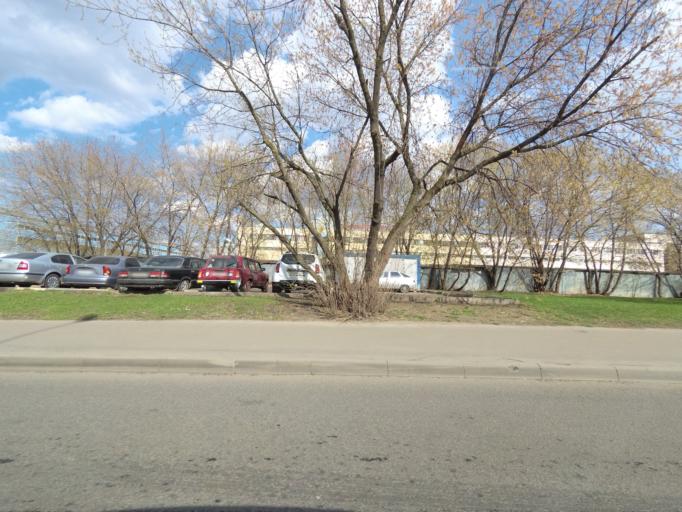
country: RU
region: Moscow
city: Gol'yanovo
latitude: 55.8034
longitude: 37.8304
